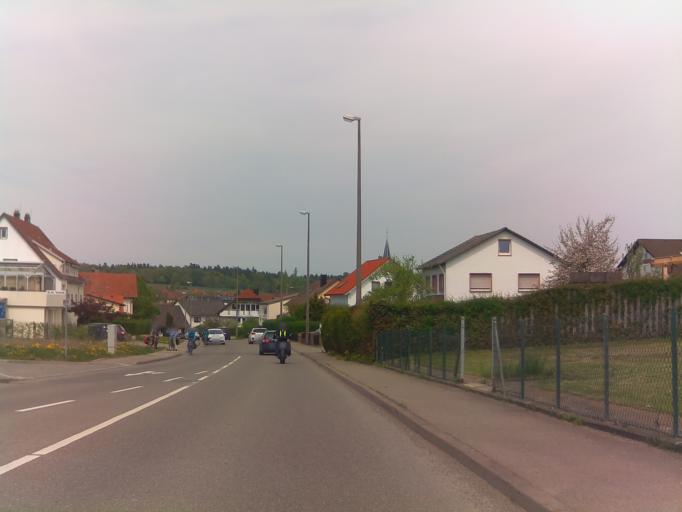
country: DE
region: Baden-Wuerttemberg
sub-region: Freiburg Region
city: Deisslingen
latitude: 48.1069
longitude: 8.6022
